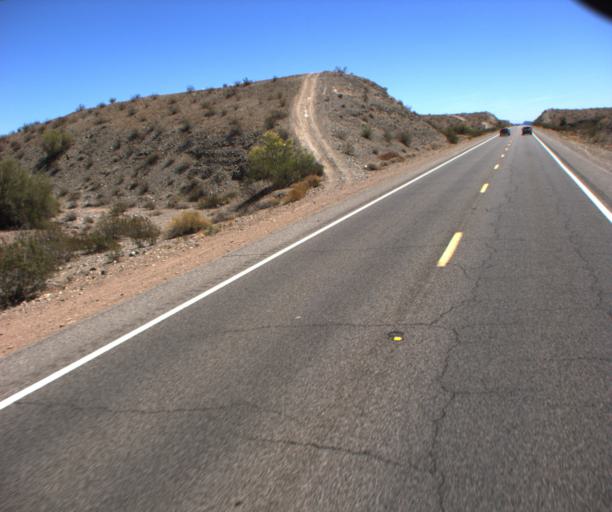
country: US
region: Arizona
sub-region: Mohave County
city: Lake Havasu City
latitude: 34.4322
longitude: -114.2165
